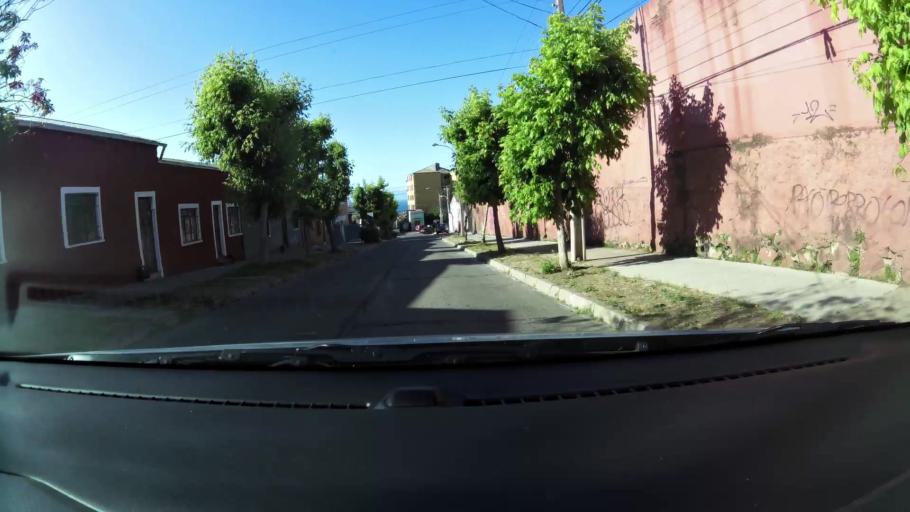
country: CL
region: Valparaiso
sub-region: Provincia de Valparaiso
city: Vina del Mar
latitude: -33.0271
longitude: -71.5687
